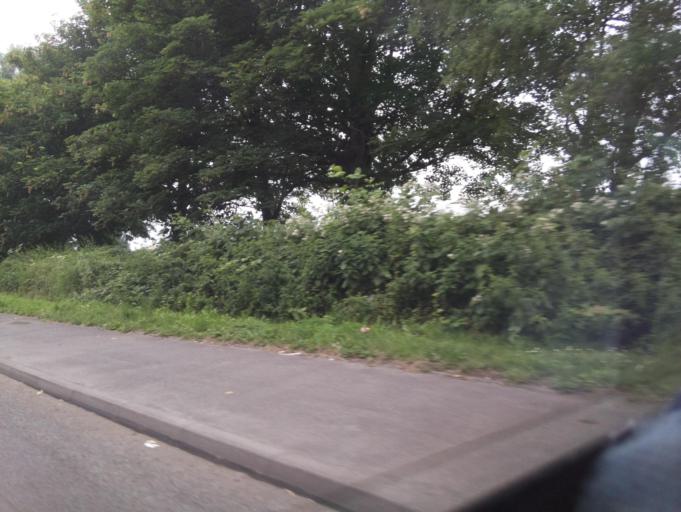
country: GB
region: England
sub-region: Staffordshire
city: Burton upon Trent
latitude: 52.8302
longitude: -1.6147
